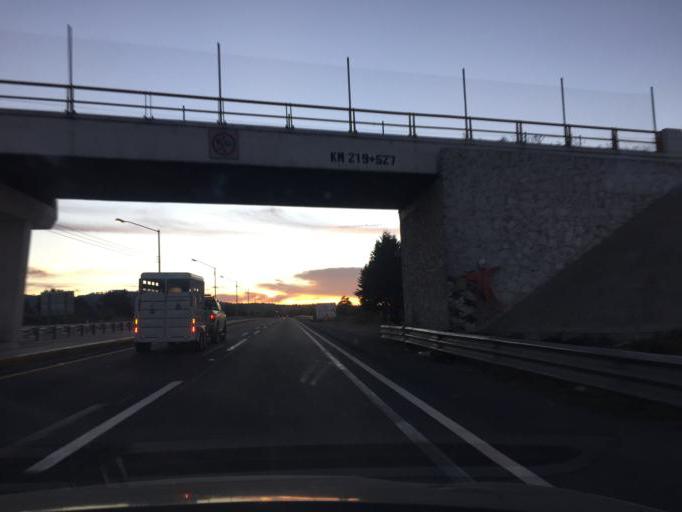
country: MX
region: Puebla
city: San Jose Esperanza
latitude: 18.8626
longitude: -97.3685
